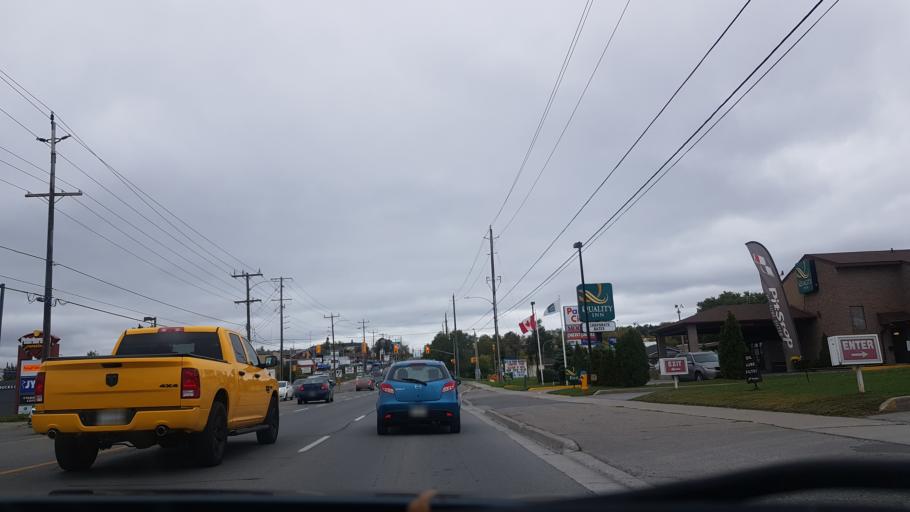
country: CA
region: Ontario
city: Peterborough
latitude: 44.2819
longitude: -78.3458
